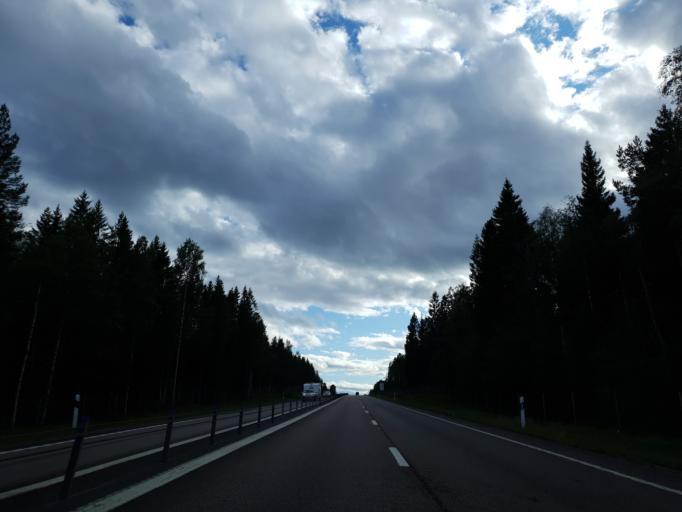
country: SE
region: Vaesternorrland
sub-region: Haernoesands Kommun
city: Haernoesand
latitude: 62.5728
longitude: 17.7455
